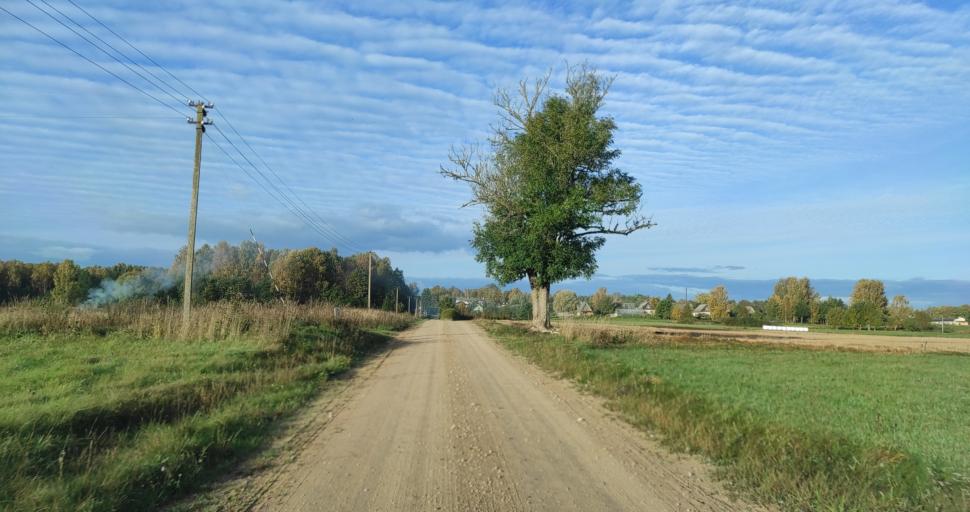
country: LV
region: Skrunda
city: Skrunda
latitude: 56.7463
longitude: 21.8949
